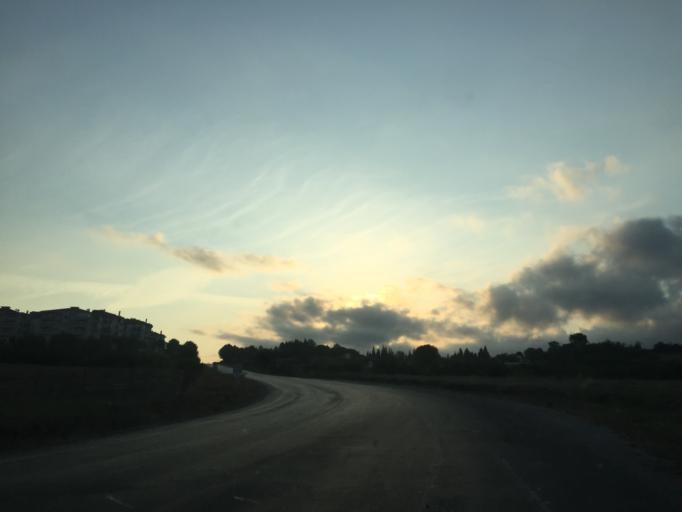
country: TR
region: Balikesir
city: Gonen
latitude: 40.0912
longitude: 27.6440
